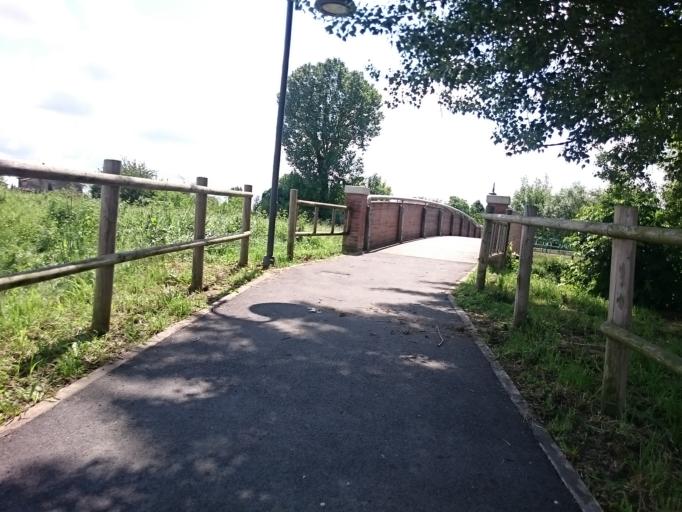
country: IT
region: Veneto
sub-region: Provincia di Padova
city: Arlesega
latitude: 45.4627
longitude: 11.7215
